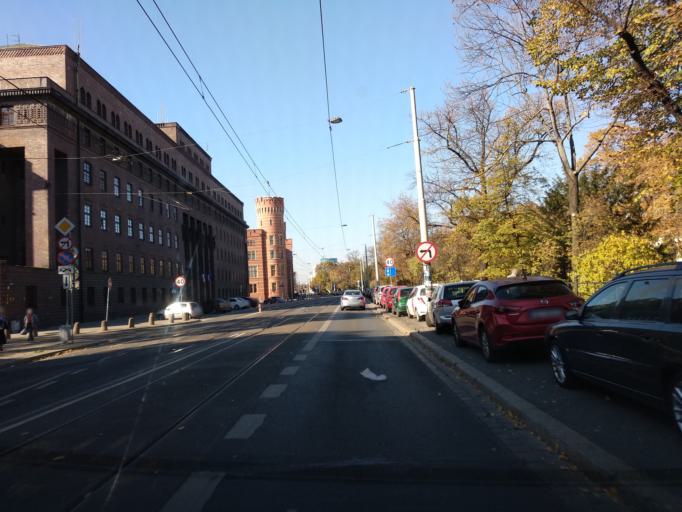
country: PL
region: Lower Silesian Voivodeship
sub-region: Powiat wroclawski
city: Wroclaw
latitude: 51.1049
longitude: 17.0290
